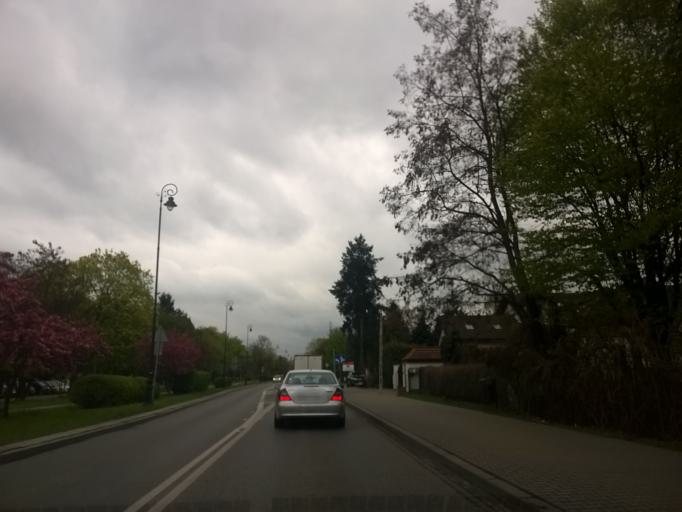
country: PL
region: Masovian Voivodeship
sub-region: Powiat piaseczynski
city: Konstancin-Jeziorna
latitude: 52.1010
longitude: 21.1149
